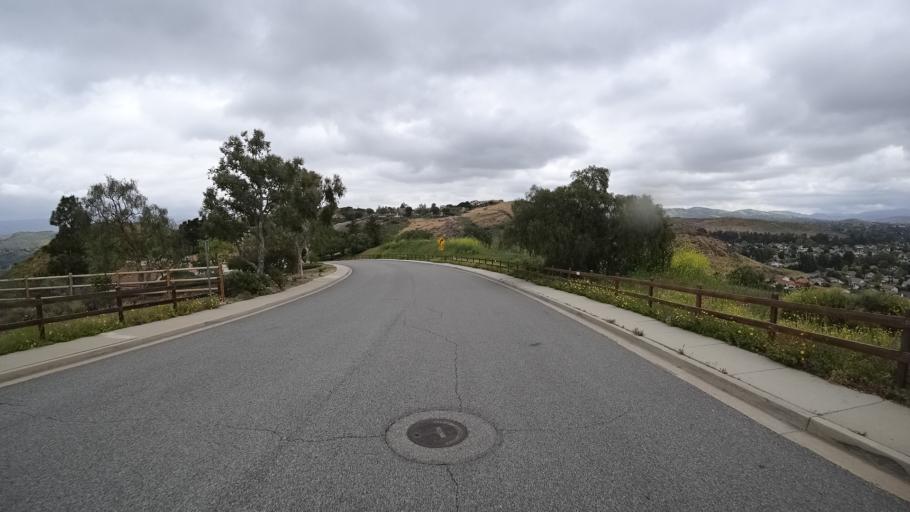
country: US
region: California
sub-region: Ventura County
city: Moorpark
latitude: 34.2276
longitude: -118.8975
